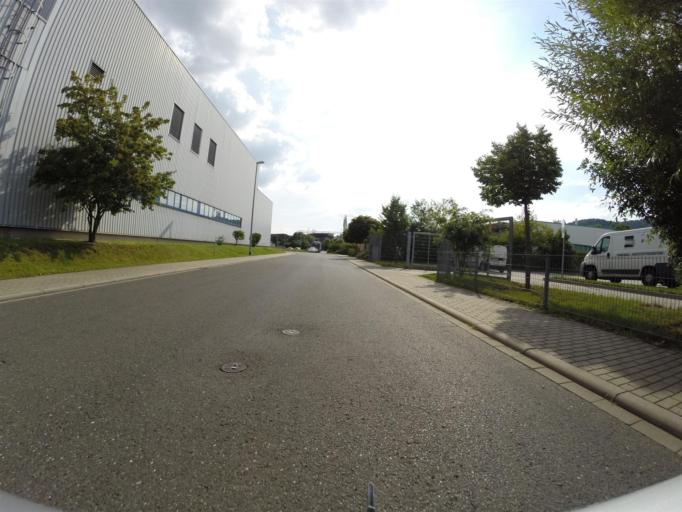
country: DE
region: Thuringia
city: Jena
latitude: 50.9455
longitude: 11.6061
